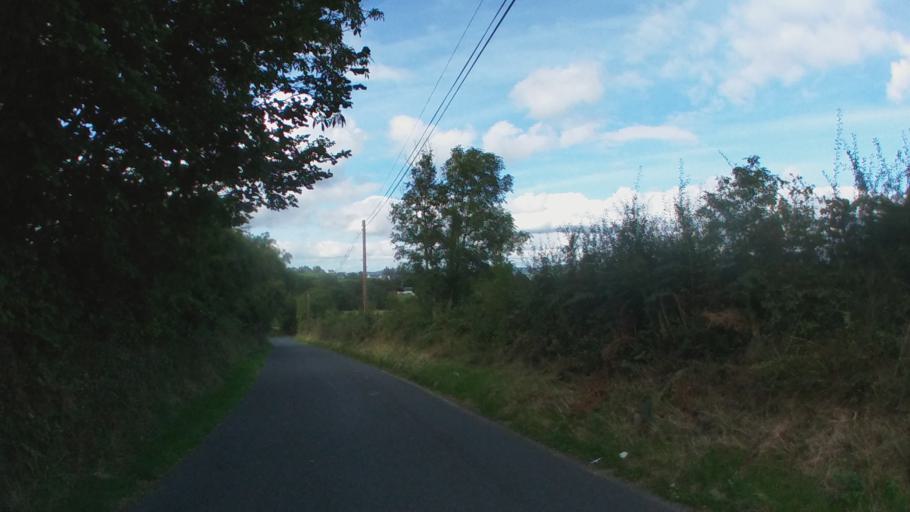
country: GB
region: Northern Ireland
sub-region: Down District
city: Warrenpoint
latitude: 54.0746
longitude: -6.2741
